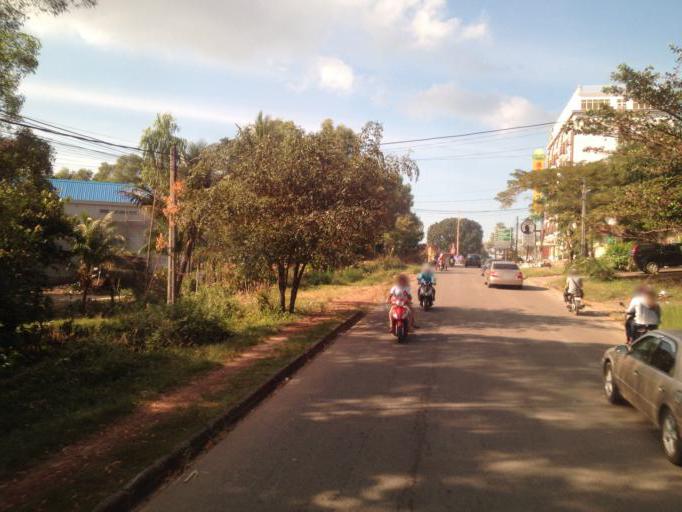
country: KH
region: Preah Sihanouk
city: Sihanoukville
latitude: 10.6327
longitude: 103.5090
